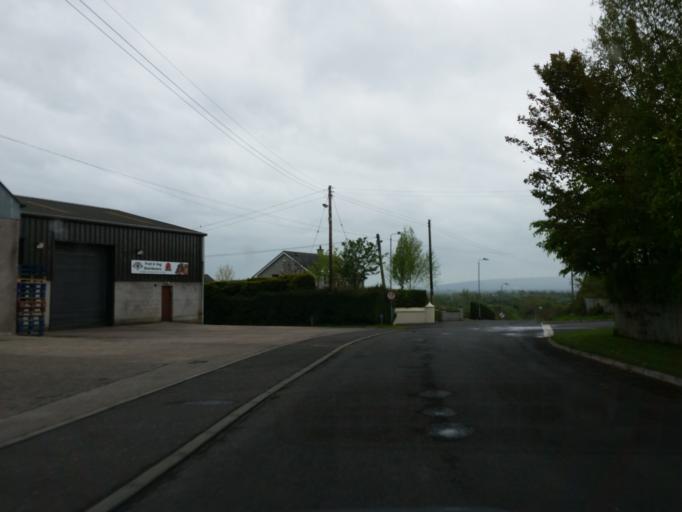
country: GB
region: Northern Ireland
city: Lisnaskea
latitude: 54.2417
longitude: -7.4415
